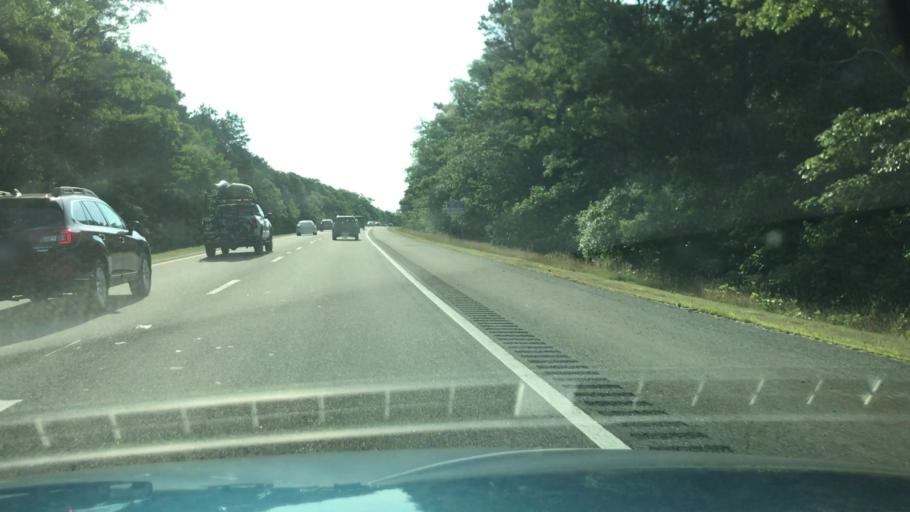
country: US
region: Massachusetts
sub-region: Barnstable County
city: Barnstable
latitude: 41.6898
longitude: -70.3200
